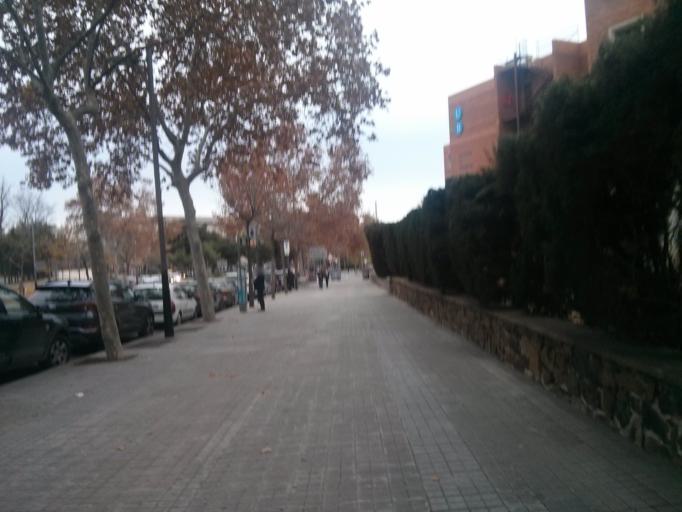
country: ES
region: Catalonia
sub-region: Provincia de Barcelona
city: les Corts
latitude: 41.3855
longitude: 2.1225
